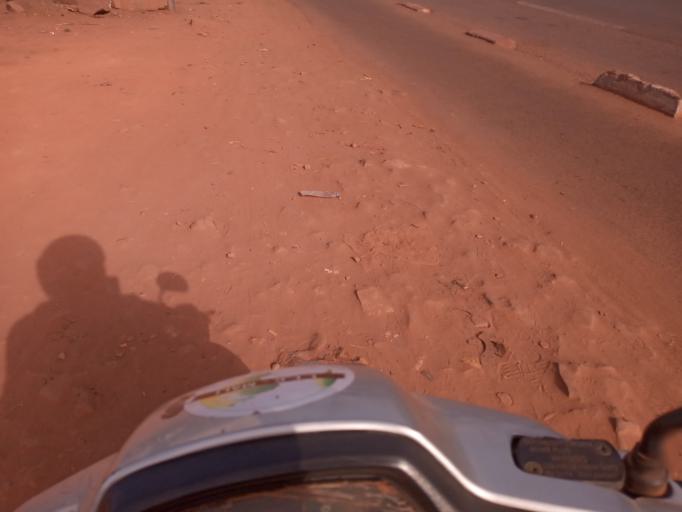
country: ML
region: Bamako
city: Bamako
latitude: 12.6054
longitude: -7.9712
